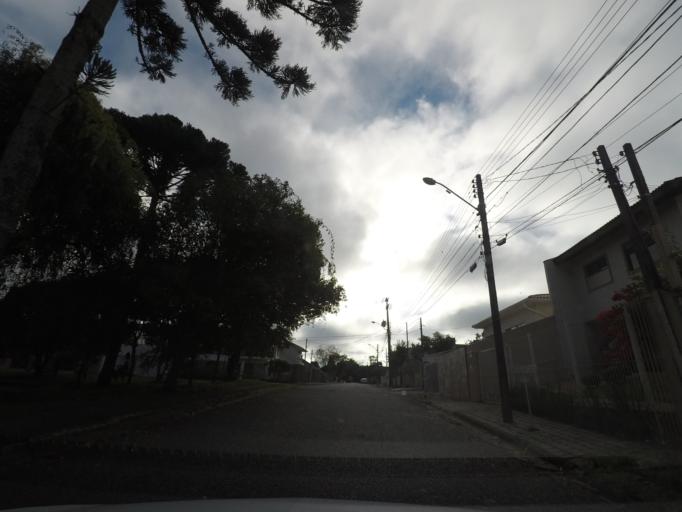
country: BR
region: Parana
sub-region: Pinhais
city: Pinhais
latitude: -25.4584
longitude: -49.2355
